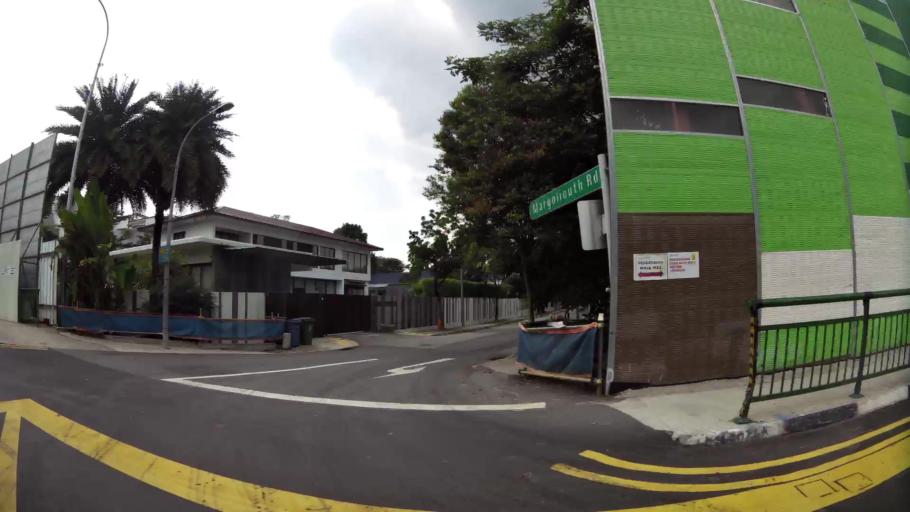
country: SG
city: Singapore
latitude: 1.3188
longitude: 103.8254
